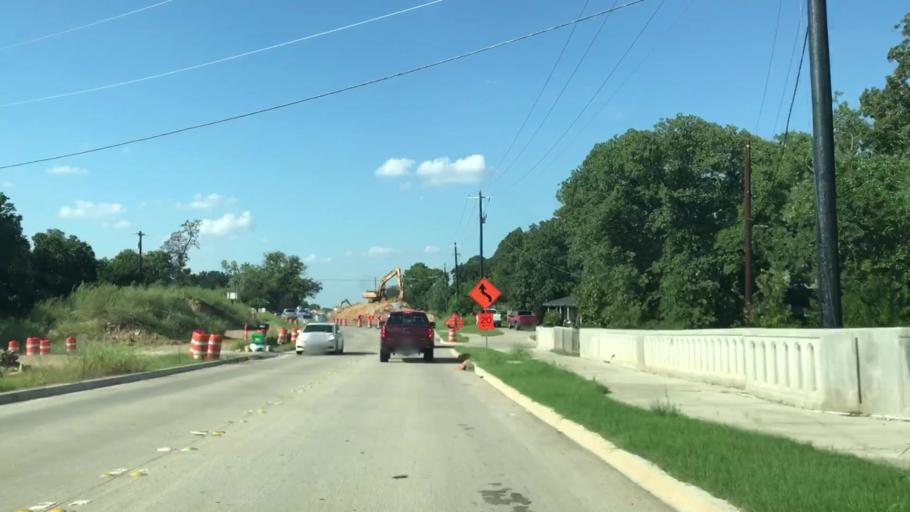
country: US
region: Texas
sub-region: Denton County
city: Trophy Club
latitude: 32.9553
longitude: -97.1854
